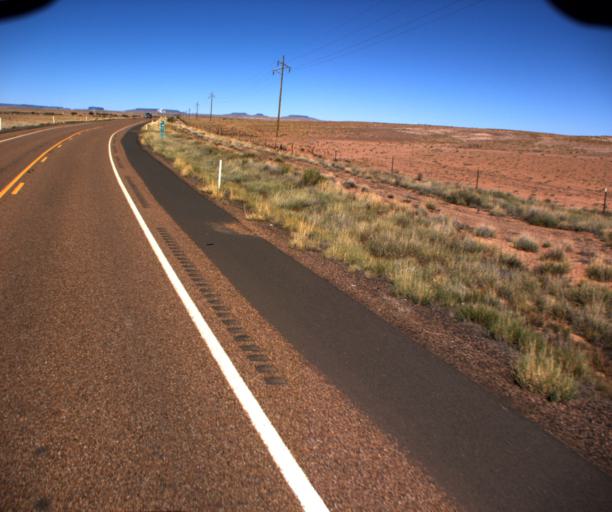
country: US
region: Arizona
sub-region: Navajo County
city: Holbrook
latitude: 35.0703
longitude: -110.1002
